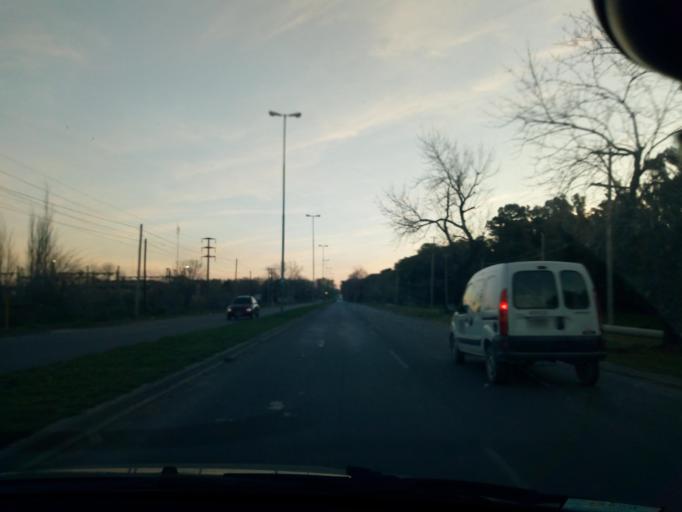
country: AR
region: Buenos Aires
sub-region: Partido de Ensenada
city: Ensenada
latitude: -34.8879
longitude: -57.9319
